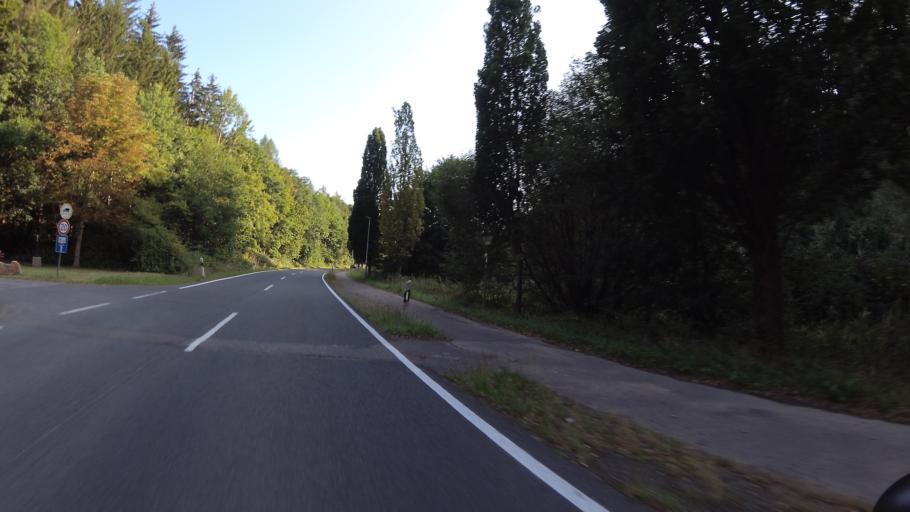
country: DE
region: Saarland
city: Blieskastel
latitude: 49.2496
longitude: 7.2451
